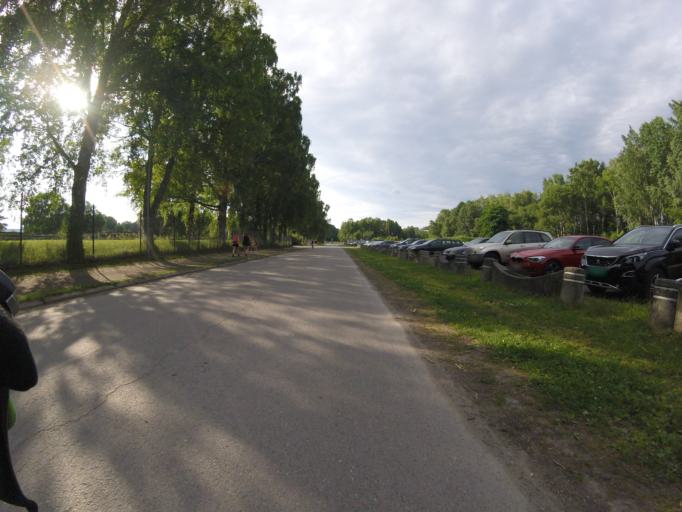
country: NO
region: Akershus
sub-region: Skedsmo
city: Lillestrom
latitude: 59.9669
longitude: 11.0289
